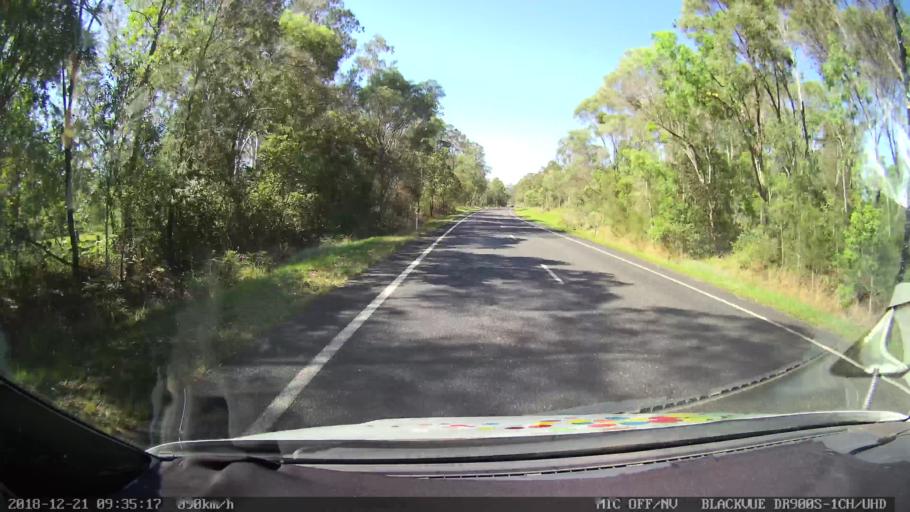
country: AU
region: New South Wales
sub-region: Clarence Valley
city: Grafton
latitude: -29.5088
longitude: 152.9819
